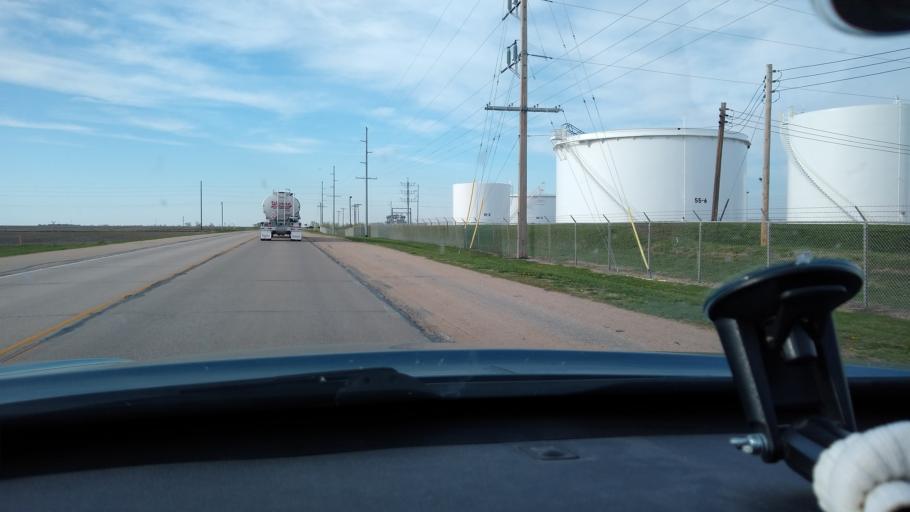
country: US
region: Nebraska
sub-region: Fillmore County
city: Geneva
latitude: 40.5509
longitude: -97.5958
